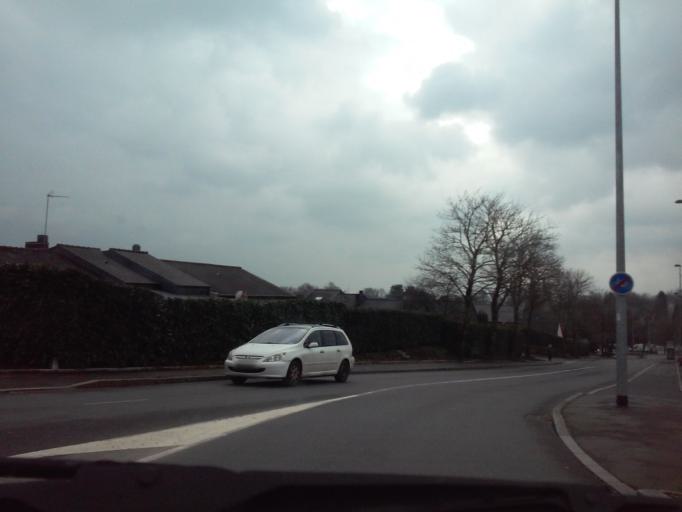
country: FR
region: Brittany
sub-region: Departement d'Ille-et-Vilaine
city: Fougeres
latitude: 48.3653
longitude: -1.1848
